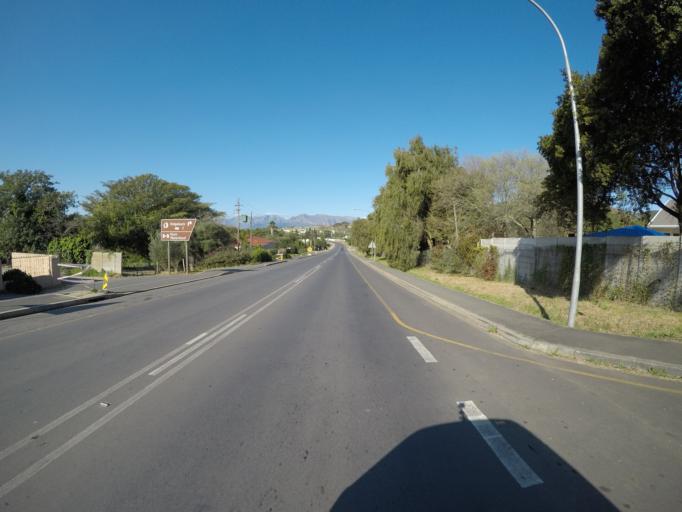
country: ZA
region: Western Cape
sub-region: Cape Winelands District Municipality
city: Noorder-Paarl
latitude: -33.6710
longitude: 18.9140
